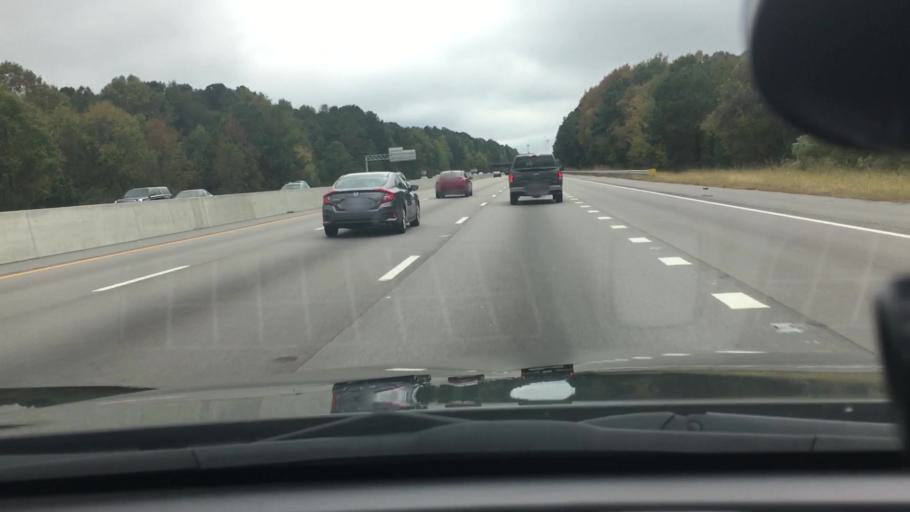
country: US
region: North Carolina
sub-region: Wake County
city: West Raleigh
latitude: 35.7534
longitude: -78.6877
